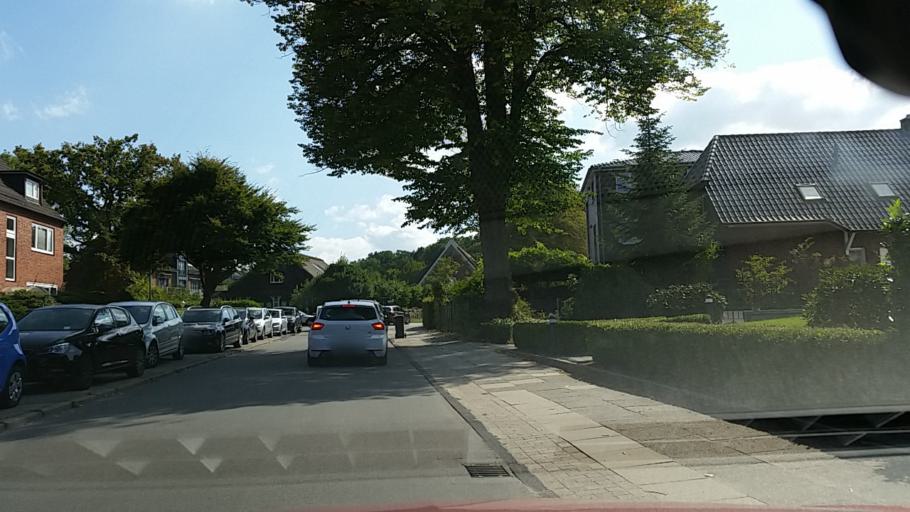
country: DE
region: Hamburg
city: Bergstedt
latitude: 53.6537
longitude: 10.1679
